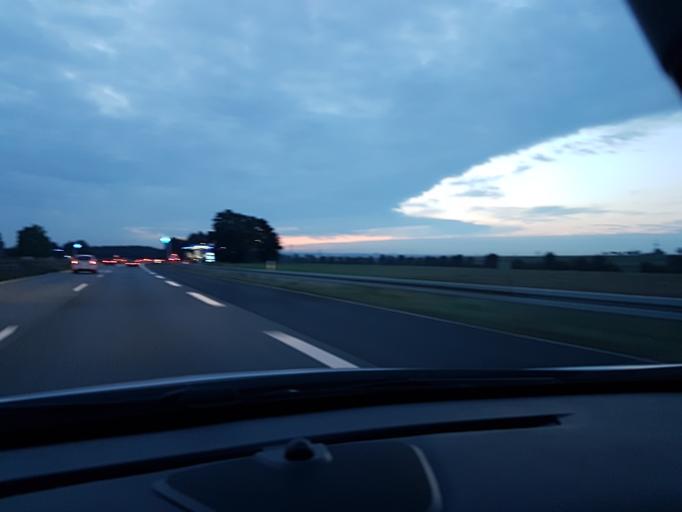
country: DE
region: Hesse
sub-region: Regierungsbezirk Darmstadt
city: Bad Homburg vor der Hoehe
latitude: 50.2092
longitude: 8.6130
